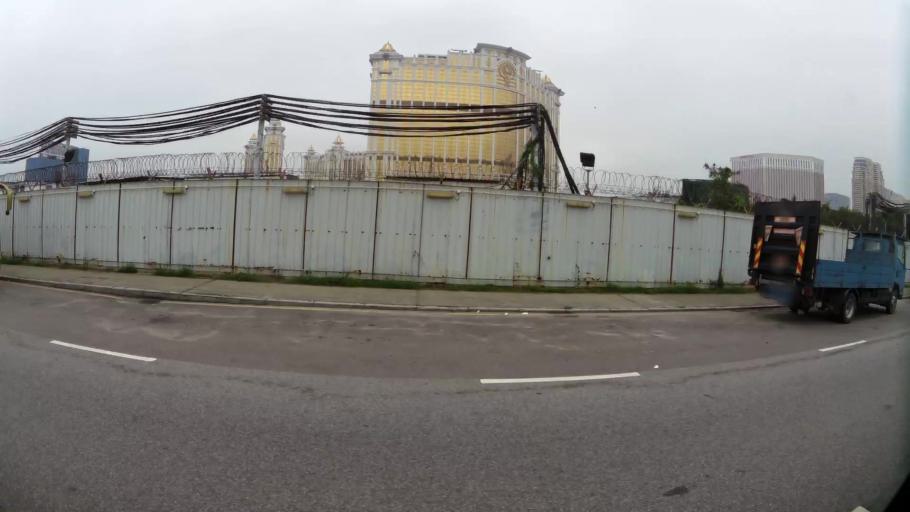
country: MO
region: Macau
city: Macau
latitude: 22.1432
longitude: 113.5543
